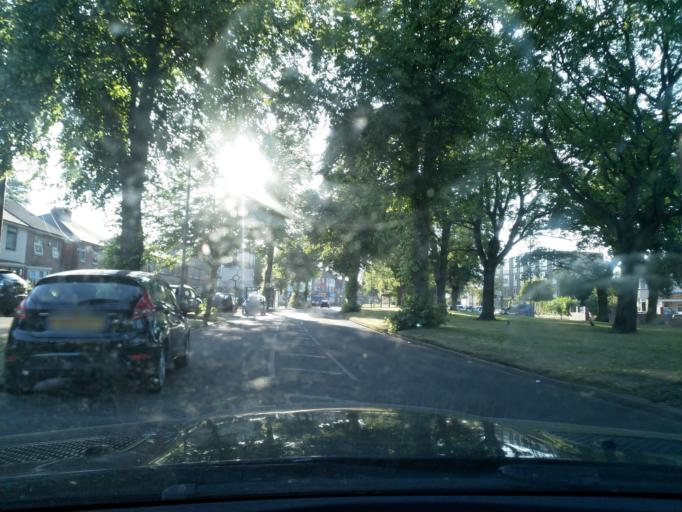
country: GB
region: England
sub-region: City and Borough of Birmingham
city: Acocks Green
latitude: 52.4425
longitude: -1.8315
